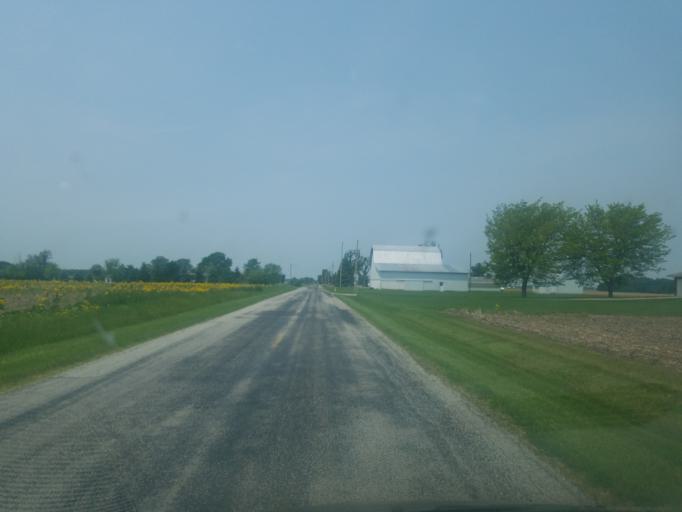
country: US
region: Ohio
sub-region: Crawford County
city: Bucyrus
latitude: 40.6887
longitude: -83.0208
